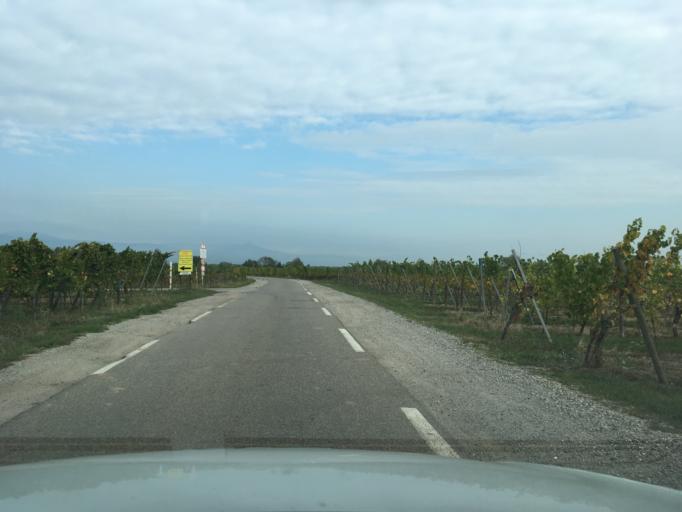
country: FR
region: Alsace
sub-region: Departement du Haut-Rhin
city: Colmar
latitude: 48.0967
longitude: 7.3460
